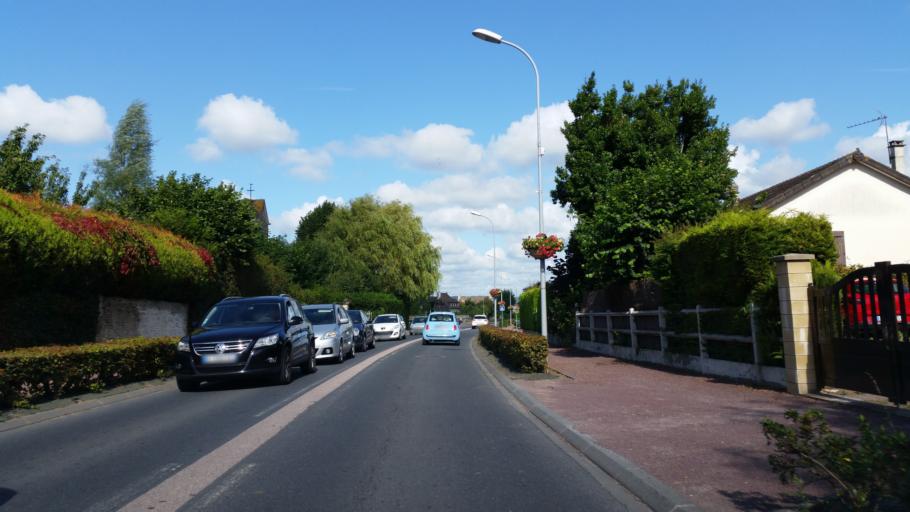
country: FR
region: Lower Normandy
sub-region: Departement du Calvados
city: Bavent
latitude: 49.2535
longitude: -0.1601
